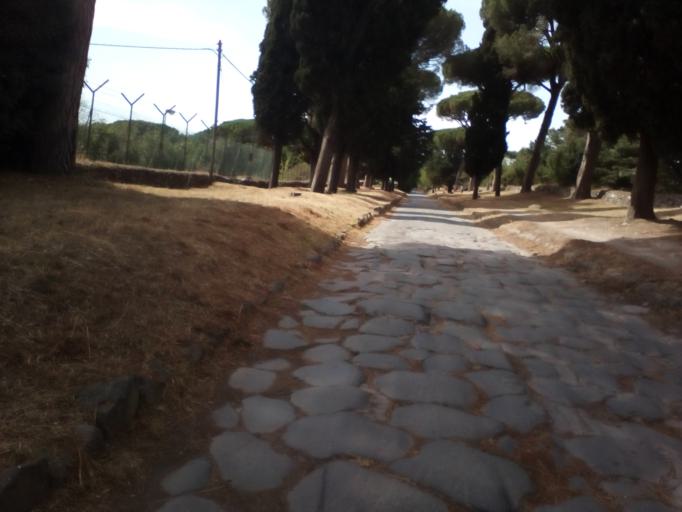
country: IT
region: Latium
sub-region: Citta metropolitana di Roma Capitale
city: Rome
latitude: 41.8437
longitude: 12.5300
